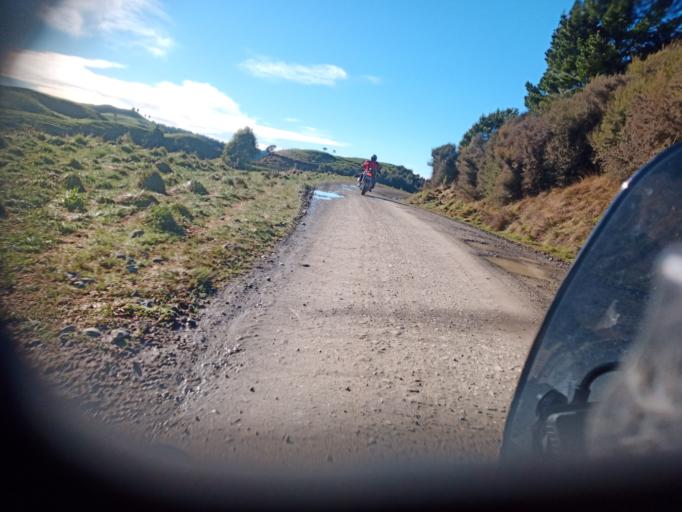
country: NZ
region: Gisborne
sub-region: Gisborne District
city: Gisborne
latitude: -38.2009
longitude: 178.0734
